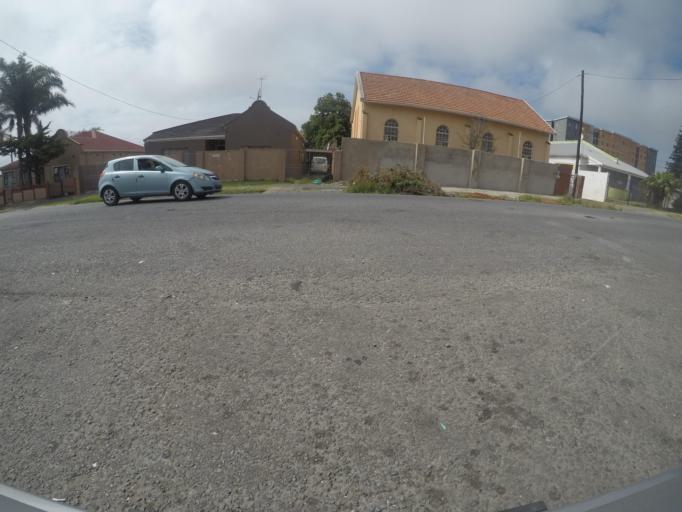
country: ZA
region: Eastern Cape
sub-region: Buffalo City Metropolitan Municipality
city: East London
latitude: -33.0004
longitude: 27.9091
